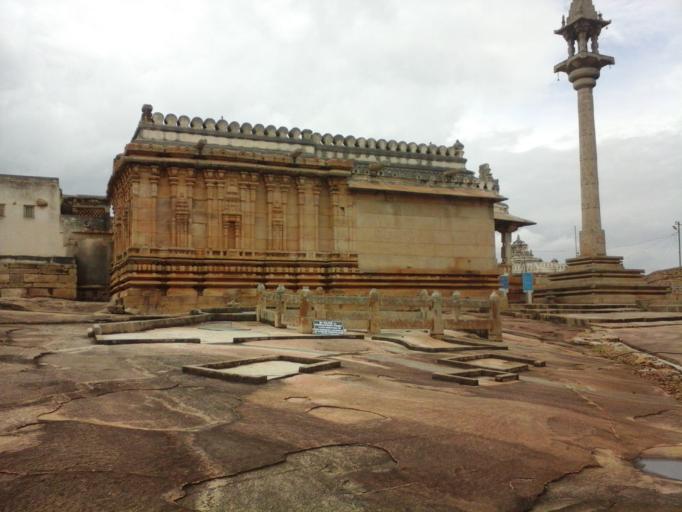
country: IN
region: Karnataka
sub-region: Hassan
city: Shravanabelagola
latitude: 12.8610
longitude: 76.4870
